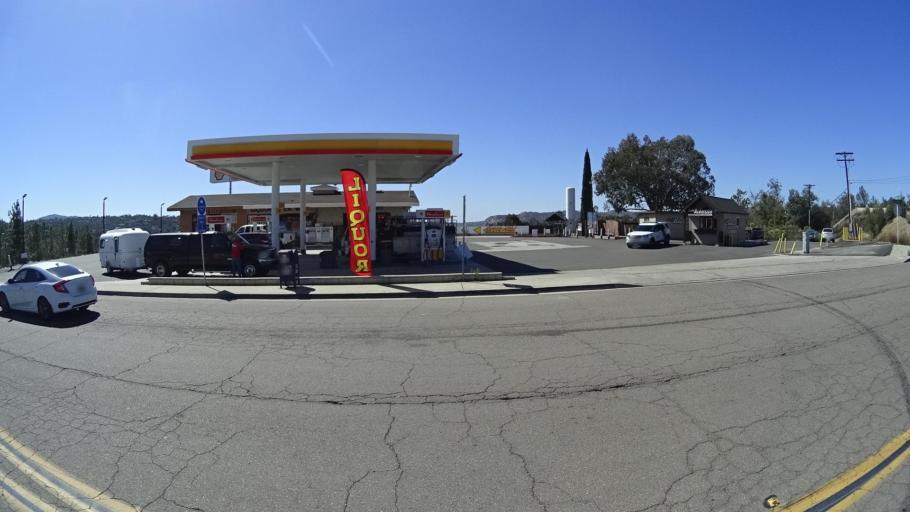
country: US
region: California
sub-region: San Diego County
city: Alpine
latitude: 32.8416
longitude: -116.7807
